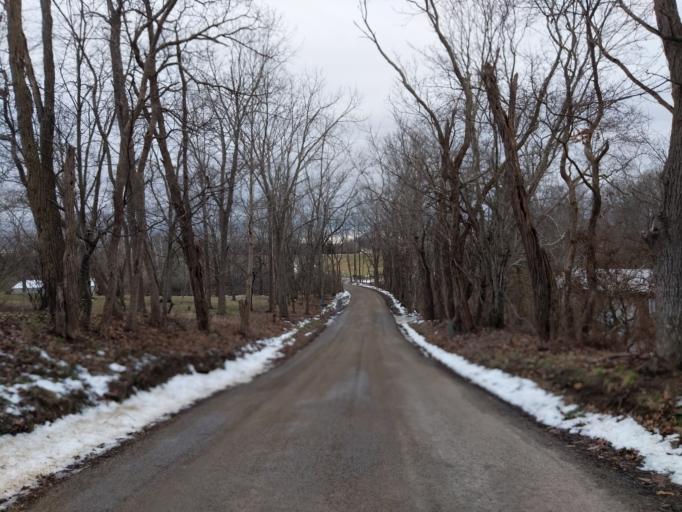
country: US
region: Ohio
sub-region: Athens County
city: The Plains
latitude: 39.3230
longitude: -82.1555
